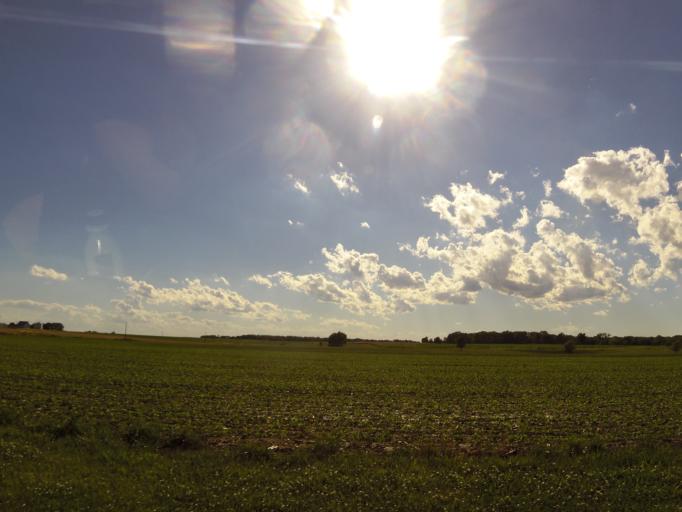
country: US
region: Missouri
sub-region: Marion County
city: Hannibal
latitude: 39.7264
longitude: -91.4483
